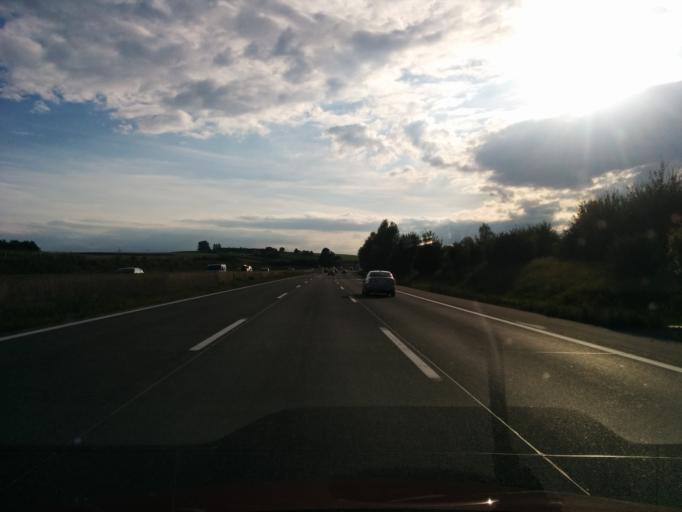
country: AT
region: Lower Austria
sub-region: Politischer Bezirk Melk
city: Erlauf
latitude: 48.1656
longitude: 15.1627
